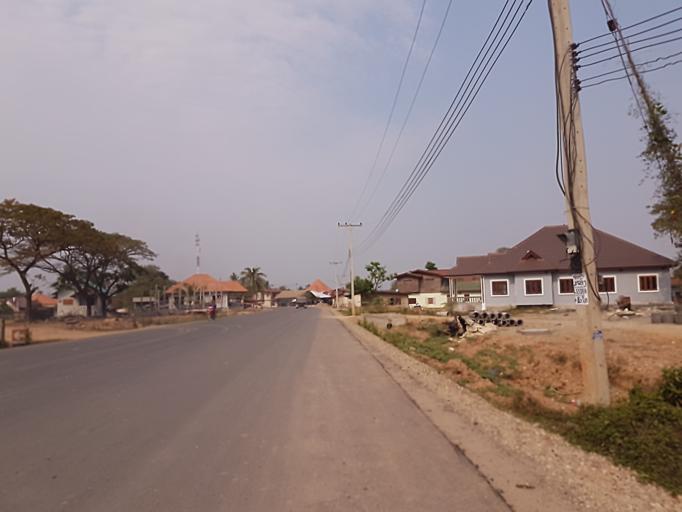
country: TH
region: Nong Khai
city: Nong Khai
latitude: 17.9652
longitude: 102.8383
